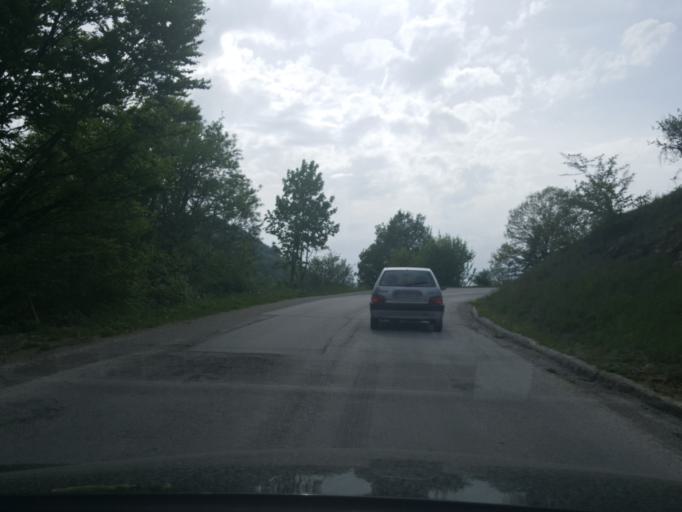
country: RS
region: Central Serbia
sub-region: Zlatiborski Okrug
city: Bajina Basta
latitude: 44.1024
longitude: 19.6679
